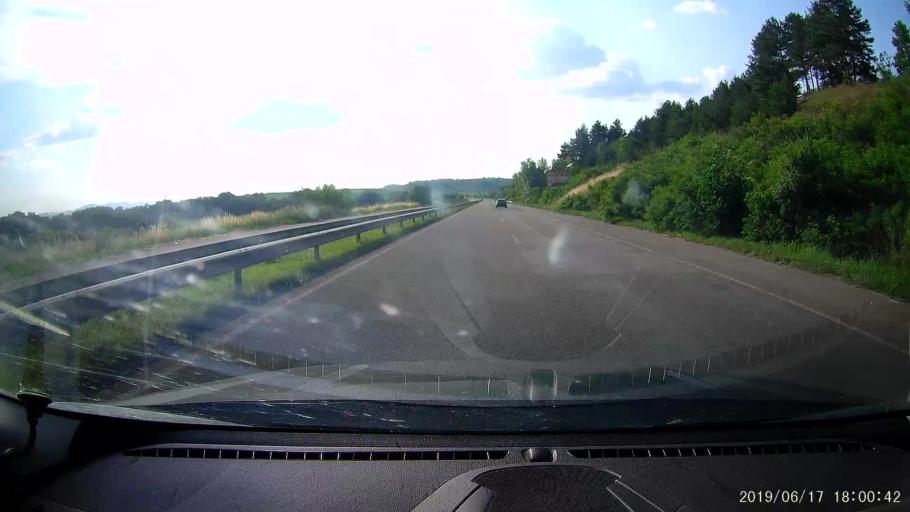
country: BG
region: Khaskovo
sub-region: Obshtina Svilengrad
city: Svilengrad
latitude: 41.7396
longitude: 26.2738
